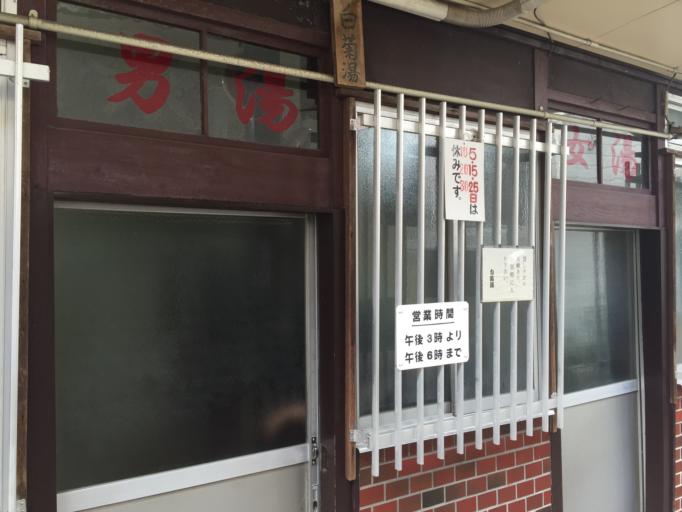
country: JP
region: Nagasaki
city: Nagasaki-shi
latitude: 32.7533
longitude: 129.8851
